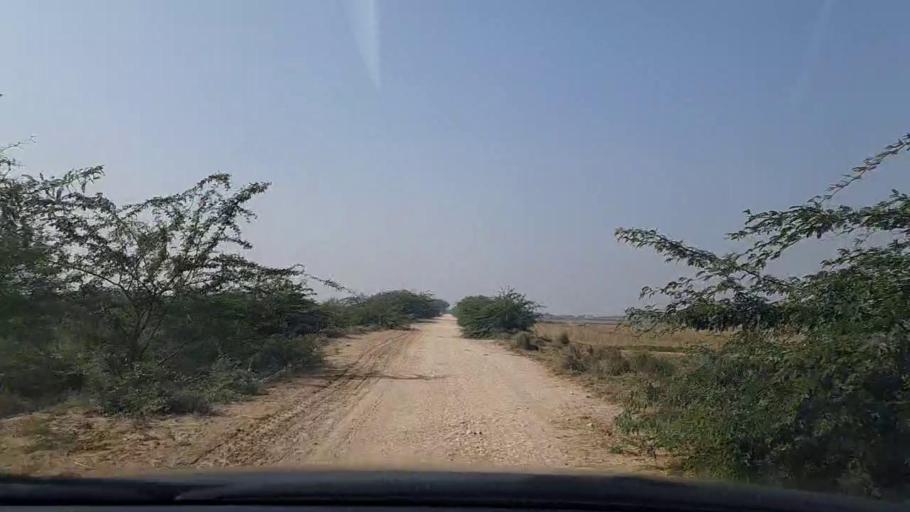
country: PK
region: Sindh
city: Mirpur Sakro
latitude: 24.5750
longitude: 67.7804
